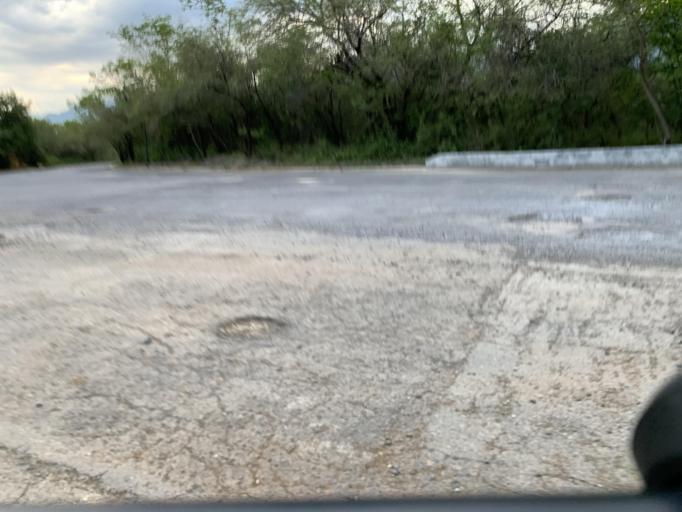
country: MX
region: Nuevo Leon
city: Santiago
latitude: 25.5089
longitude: -100.1798
